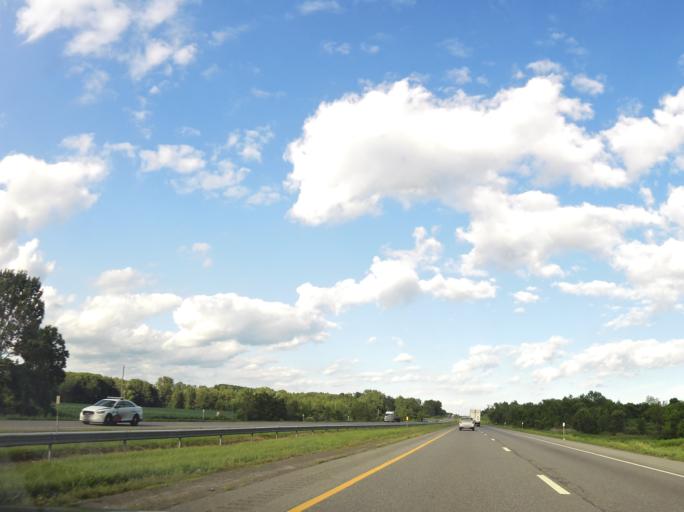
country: US
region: New York
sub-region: Genesee County
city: Oakfield
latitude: 43.0138
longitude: -78.3119
